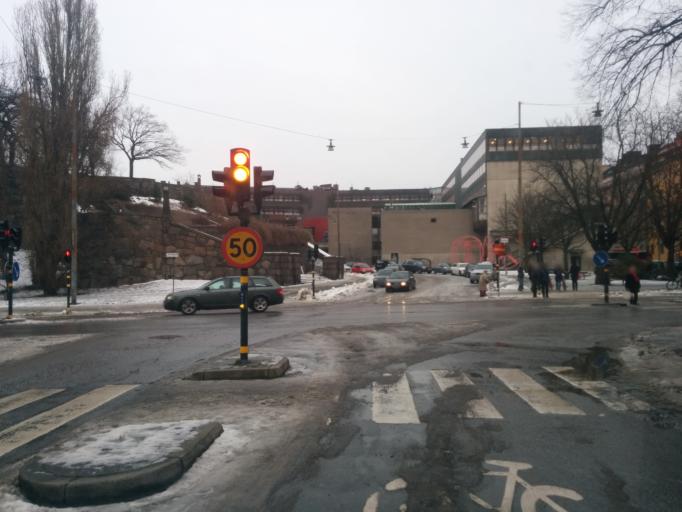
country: SE
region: Stockholm
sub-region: Stockholms Kommun
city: Stockholm
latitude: 59.3432
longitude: 18.0672
